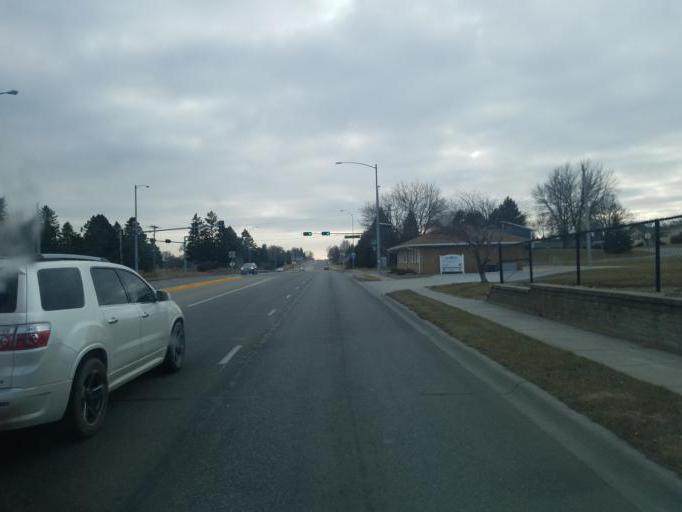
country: US
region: Nebraska
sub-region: Madison County
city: Norfolk
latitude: 42.0442
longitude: -97.4268
